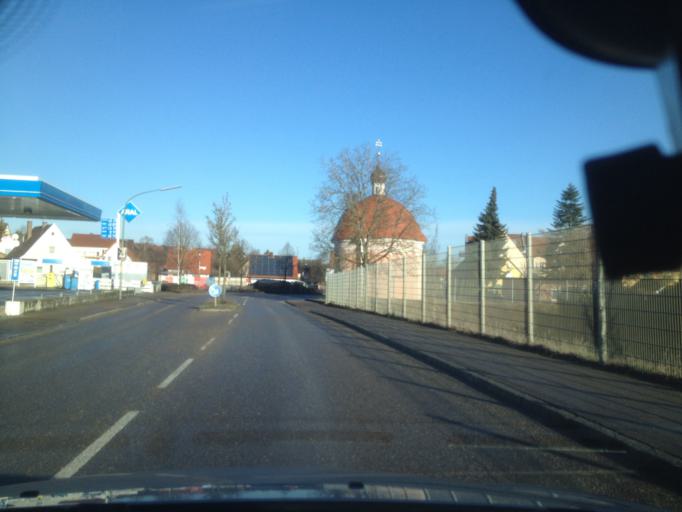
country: DE
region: Bavaria
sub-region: Swabia
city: Offingen
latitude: 48.4781
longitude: 10.3632
